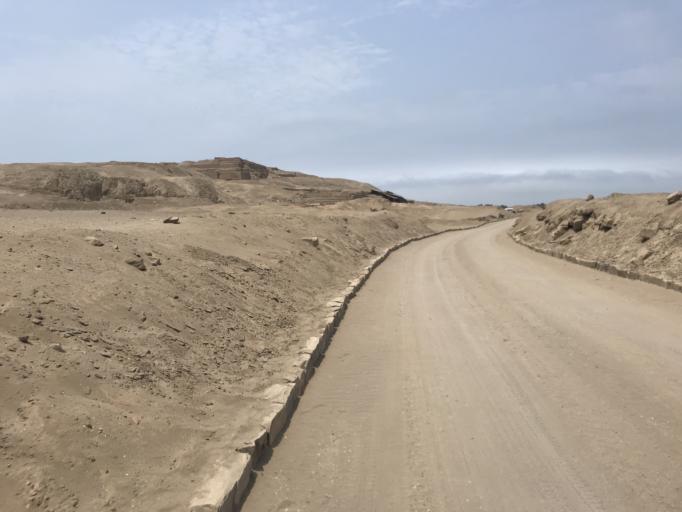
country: PE
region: Lima
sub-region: Lima
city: Punta Hermosa
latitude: -12.2583
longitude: -76.8986
